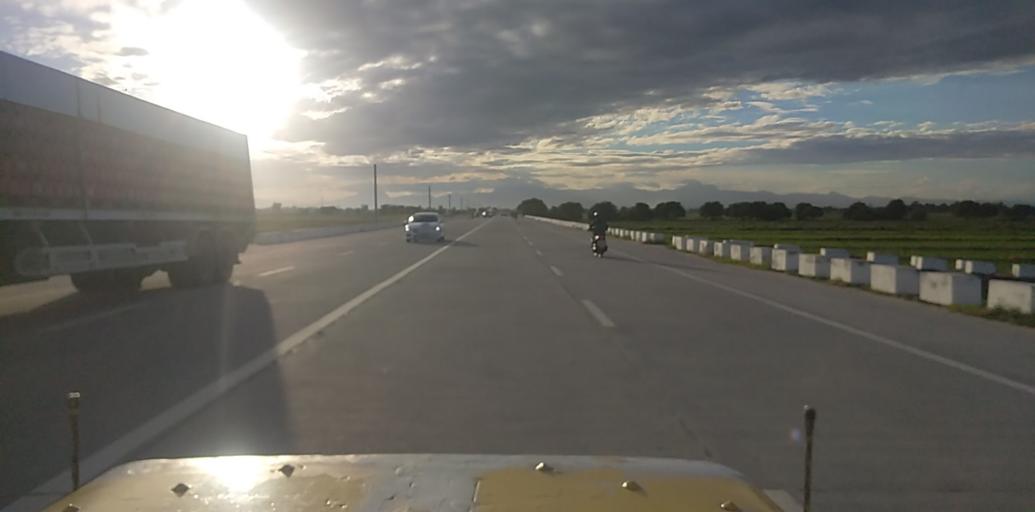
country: PH
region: Central Luzon
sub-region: Province of Pampanga
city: Anao
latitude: 15.1361
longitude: 120.6906
